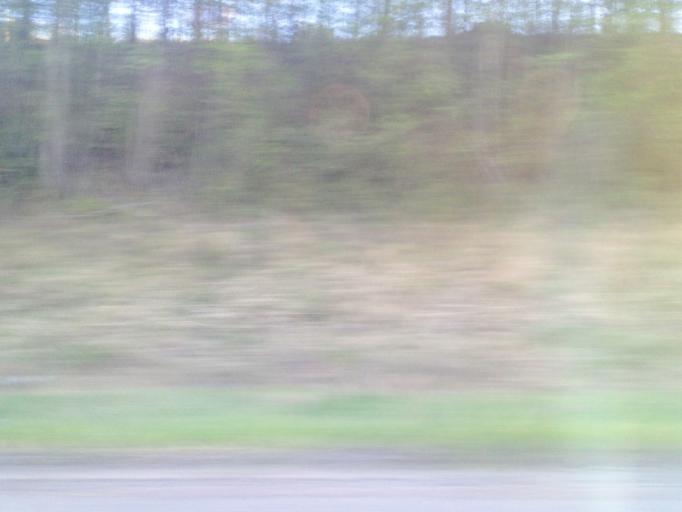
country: FI
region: Haeme
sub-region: Haemeenlinna
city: Parola
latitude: 61.0370
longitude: 24.3803
